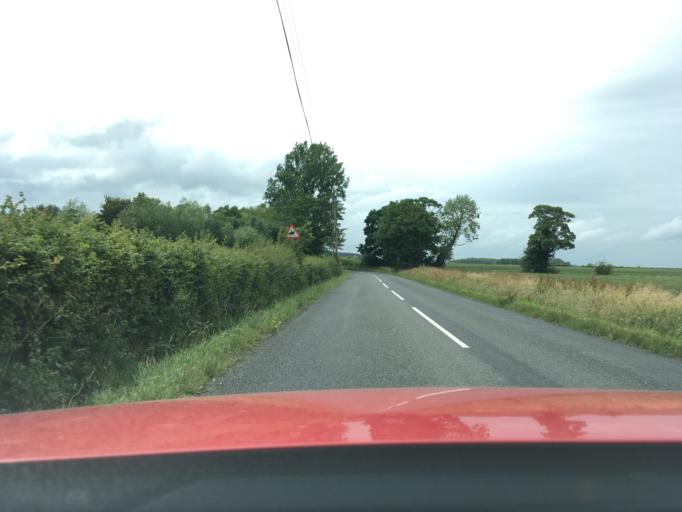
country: GB
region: England
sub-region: Worcestershire
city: Badsey
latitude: 52.0503
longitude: -1.9058
